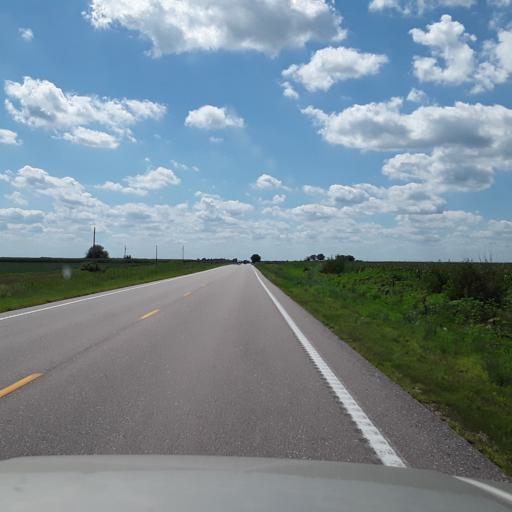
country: US
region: Nebraska
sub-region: Merrick County
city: Central City
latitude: 41.1914
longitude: -98.0644
